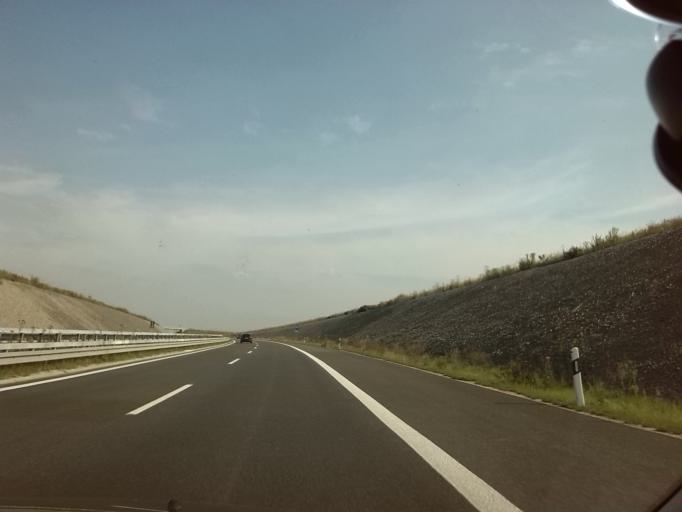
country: DE
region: Saxony
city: Geithain
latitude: 51.0286
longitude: 12.6869
